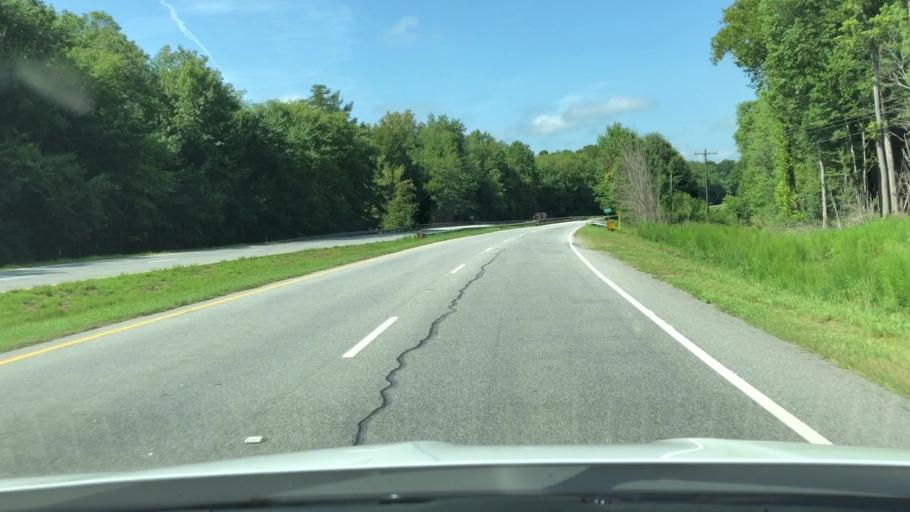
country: US
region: North Carolina
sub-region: Bertie County
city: Windsor
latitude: 35.9430
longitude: -76.9601
